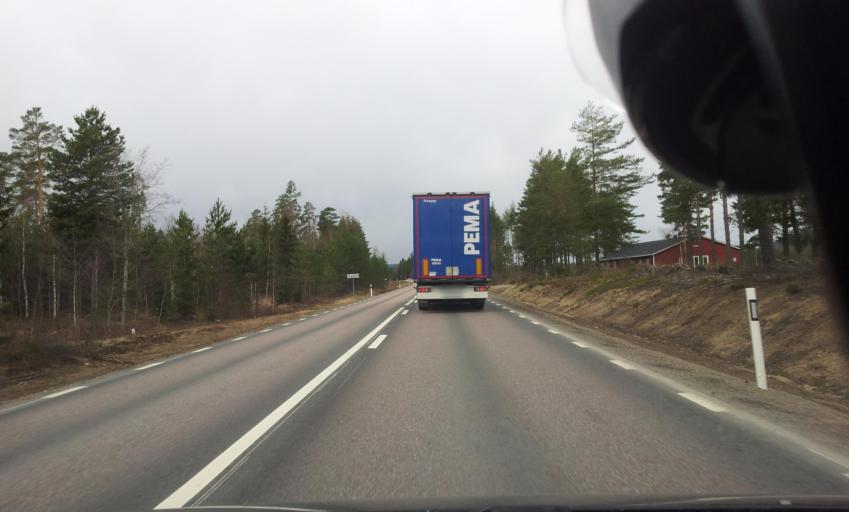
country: SE
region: Gaevleborg
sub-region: Ljusdals Kommun
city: Ljusdal
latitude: 61.8161
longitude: 16.0058
